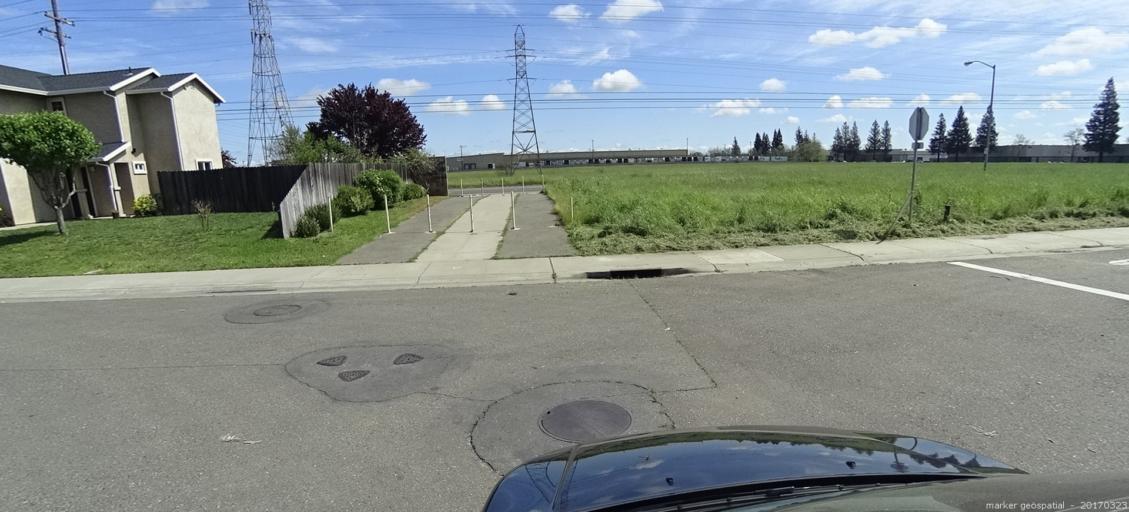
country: US
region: California
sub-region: Sacramento County
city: Florin
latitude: 38.5073
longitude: -121.4097
